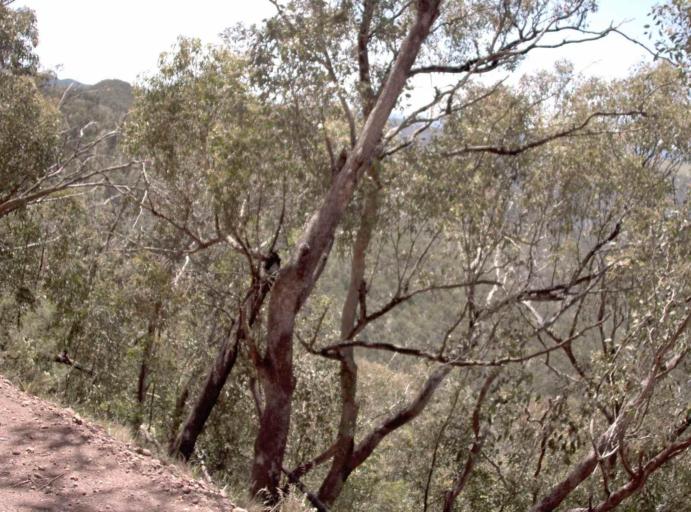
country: AU
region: New South Wales
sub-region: Snowy River
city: Jindabyne
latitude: -36.9883
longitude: 148.3022
